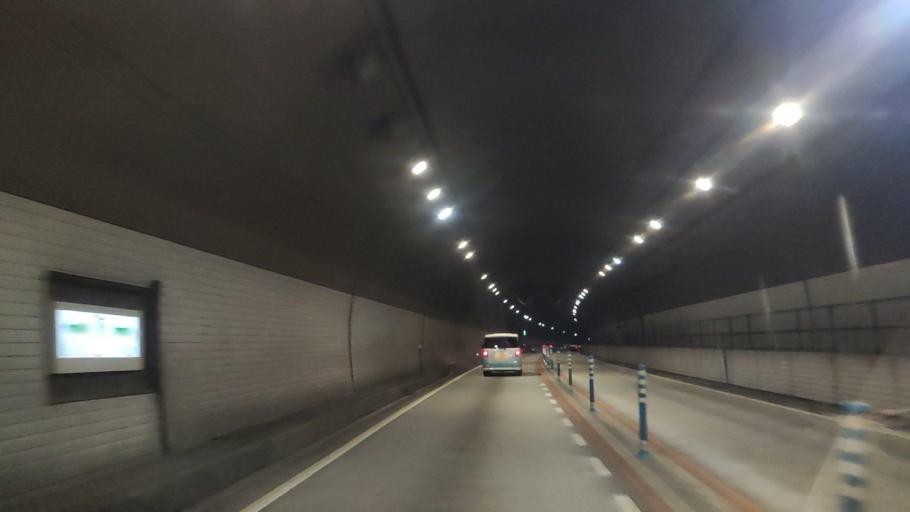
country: JP
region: Gifu
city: Takayama
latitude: 36.1724
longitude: 137.2251
